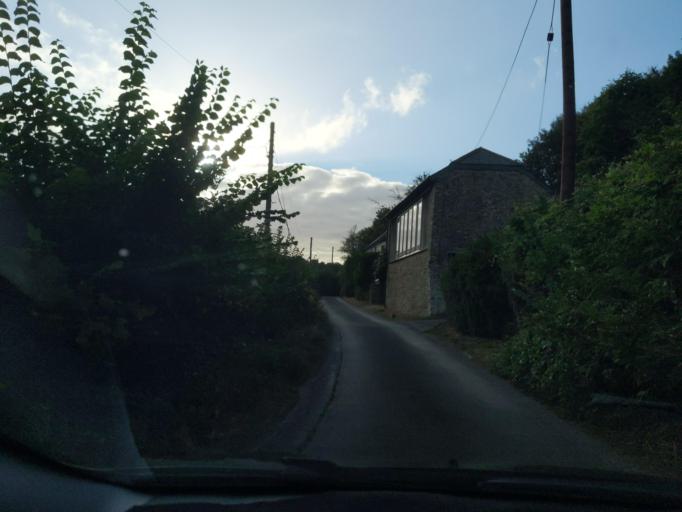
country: GB
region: England
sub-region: Devon
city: Salcombe
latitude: 50.2300
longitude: -3.7954
